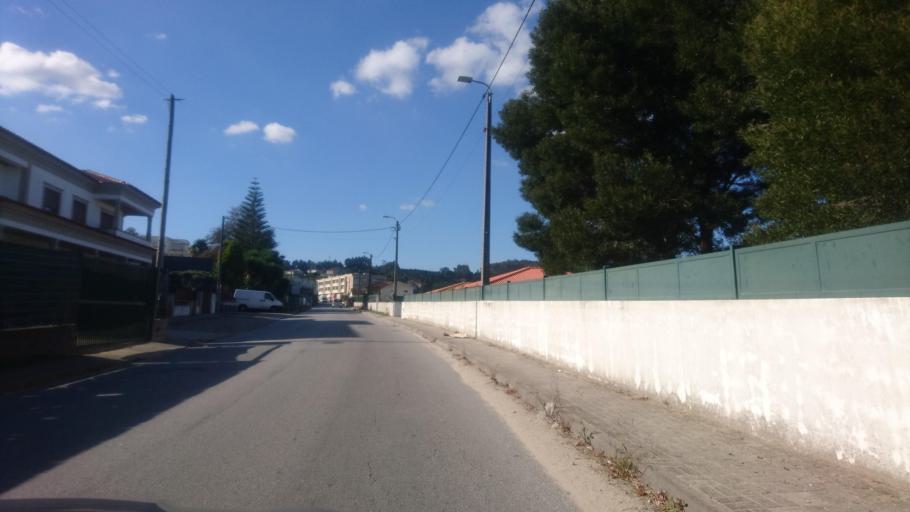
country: PT
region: Porto
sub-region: Paredes
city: Madalena
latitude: 41.2301
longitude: -8.3459
